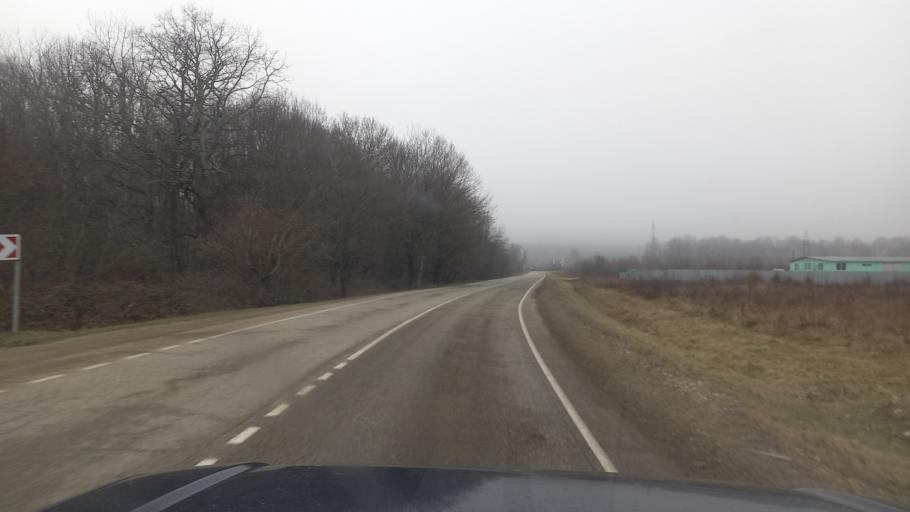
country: RU
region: Krasnodarskiy
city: Neftegorsk
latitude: 44.2878
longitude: 39.8190
